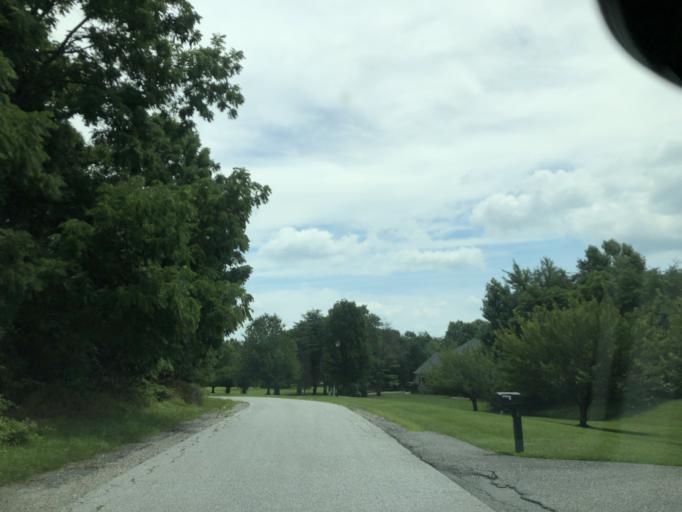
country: US
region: Maryland
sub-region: Baltimore County
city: Garrison
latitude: 39.4605
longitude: -76.7197
